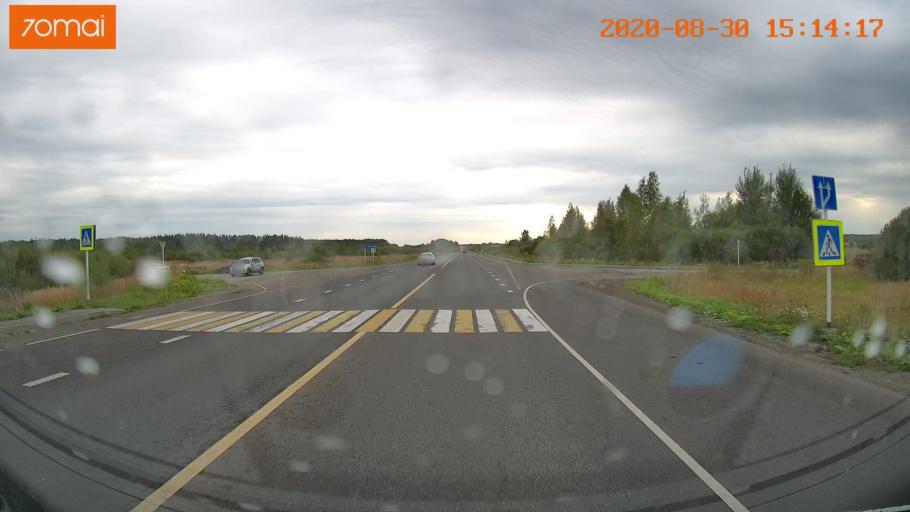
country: RU
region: Ivanovo
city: Vichuga
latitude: 57.1689
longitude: 41.8616
